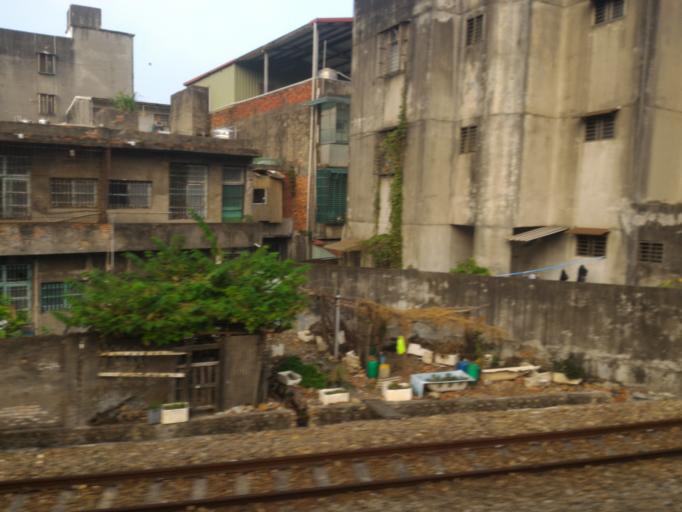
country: TW
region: Taiwan
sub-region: Taoyuan
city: Taoyuan
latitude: 24.9898
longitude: 121.3214
